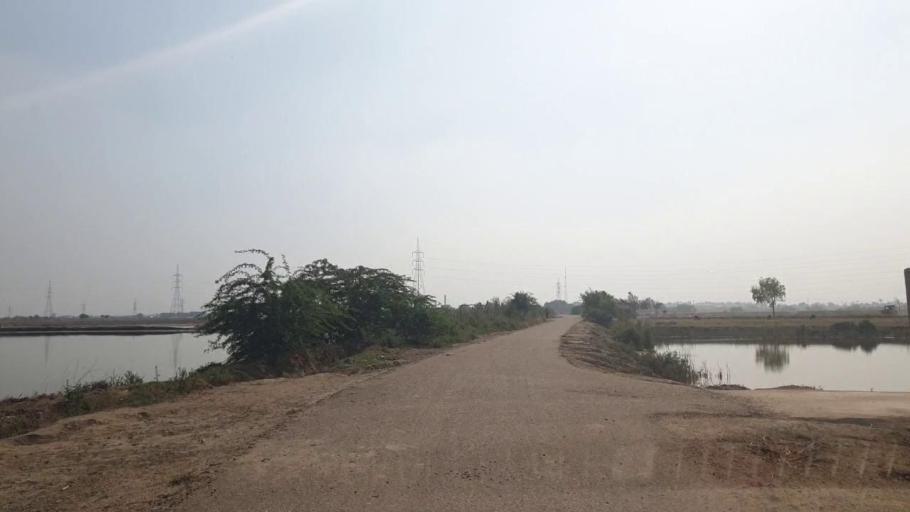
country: PK
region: Sindh
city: Jamshoro
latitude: 25.4582
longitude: 68.3368
